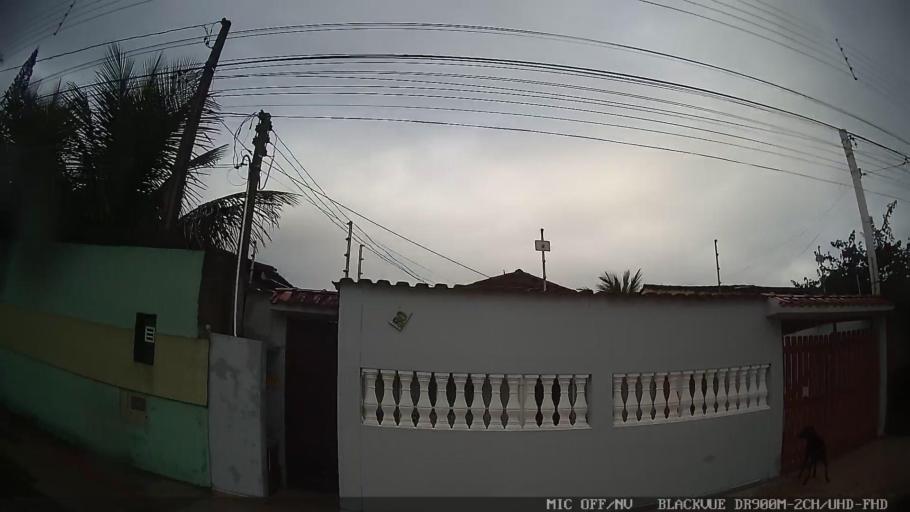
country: BR
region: Sao Paulo
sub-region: Itanhaem
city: Itanhaem
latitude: -24.1684
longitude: -46.7643
